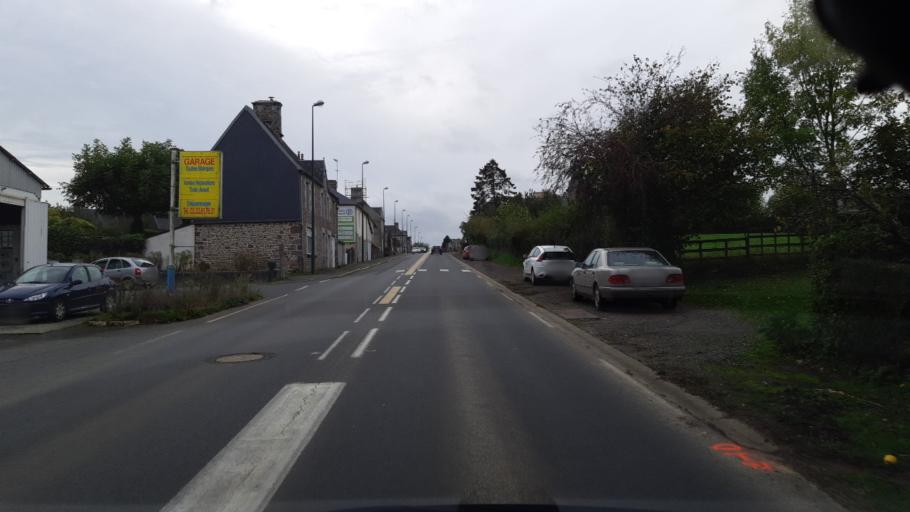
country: FR
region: Lower Normandy
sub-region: Departement de la Manche
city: Gavray
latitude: 48.9406
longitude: -1.3265
